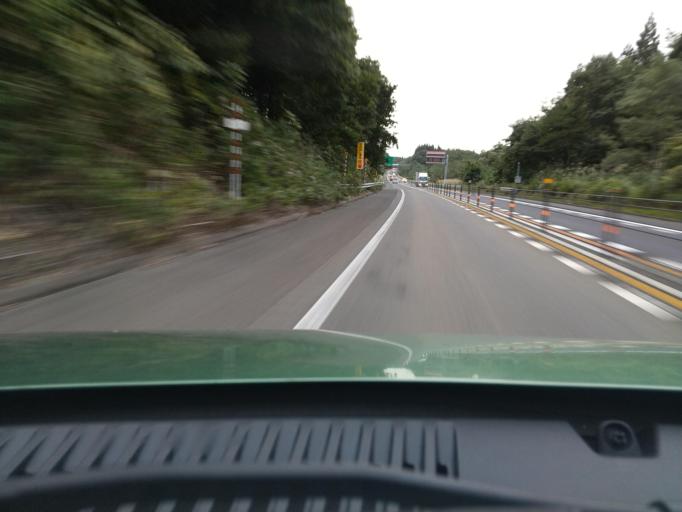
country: JP
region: Iwate
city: Kitakami
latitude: 39.2945
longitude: 140.9732
